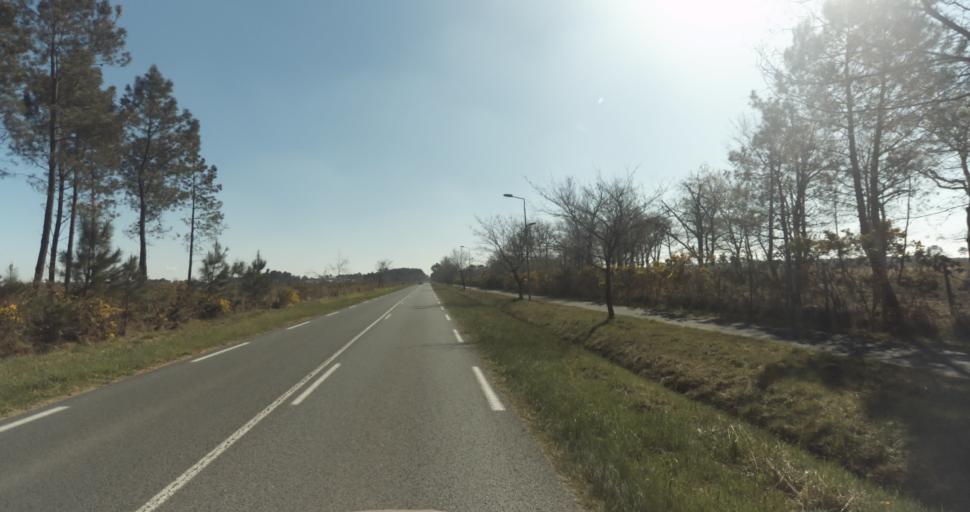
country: FR
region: Aquitaine
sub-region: Departement de la Gironde
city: Martignas-sur-Jalle
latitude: 44.8047
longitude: -0.8173
